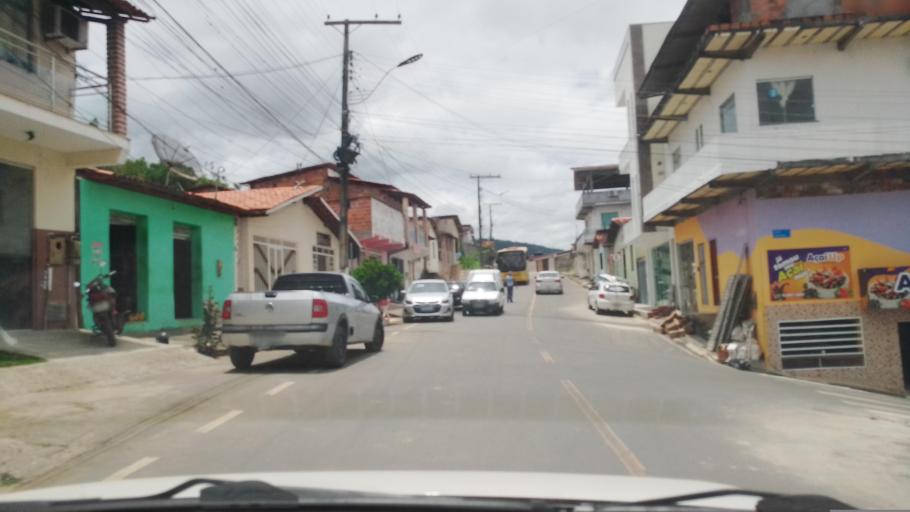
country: BR
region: Bahia
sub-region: Mutuipe
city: Mutuipe
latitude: -13.2588
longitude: -39.5689
